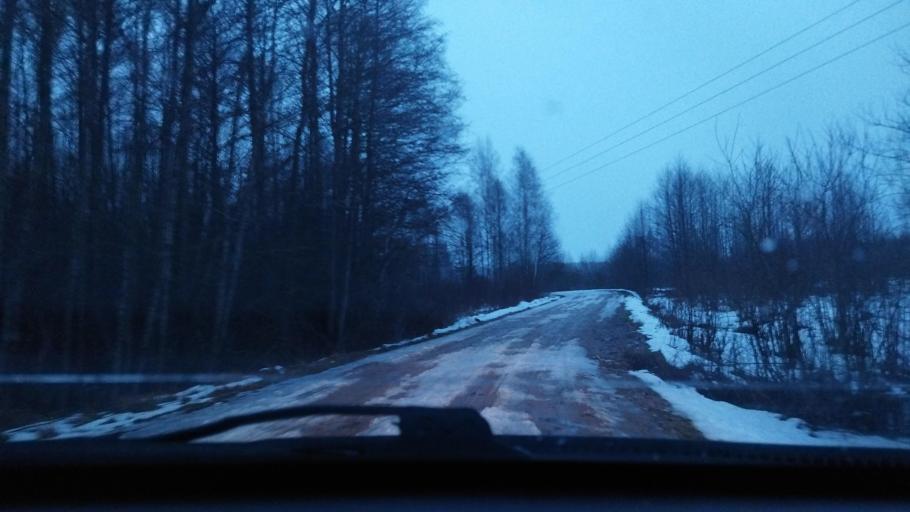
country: BY
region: Minsk
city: Svir
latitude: 54.9376
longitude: 26.3923
